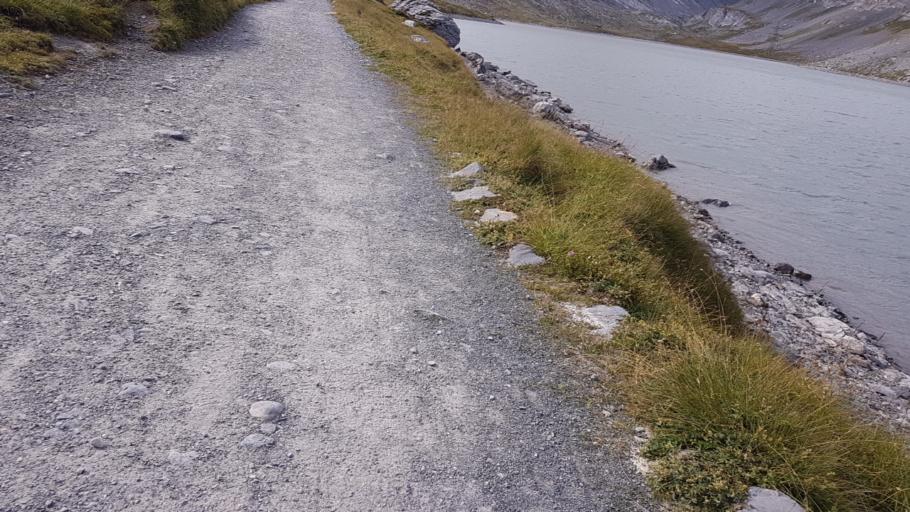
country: CH
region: Valais
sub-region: Leuk District
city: Leukerbad
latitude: 46.4168
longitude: 7.6239
